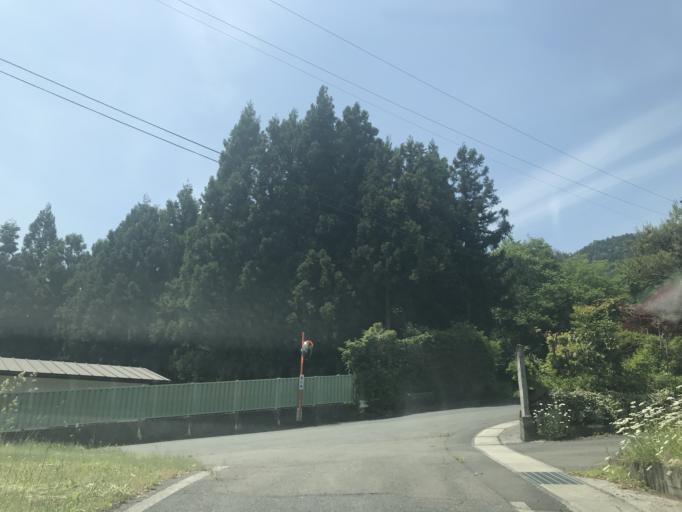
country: JP
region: Iwate
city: Ichinoseki
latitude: 38.9483
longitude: 141.2422
